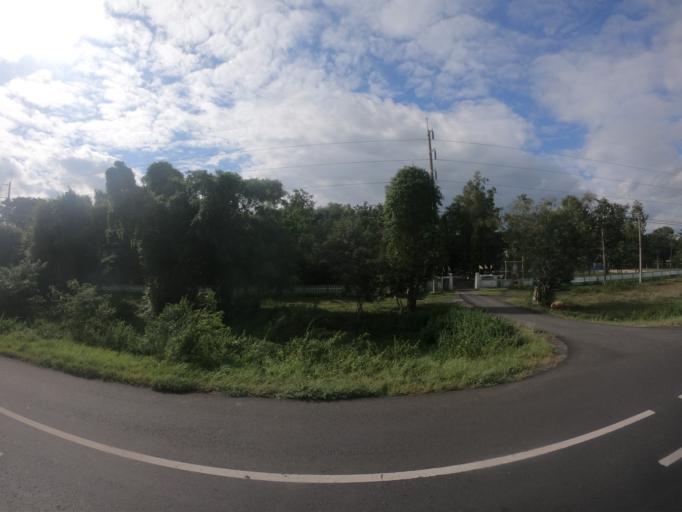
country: TH
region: Surin
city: Prasat
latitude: 14.6272
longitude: 103.3919
